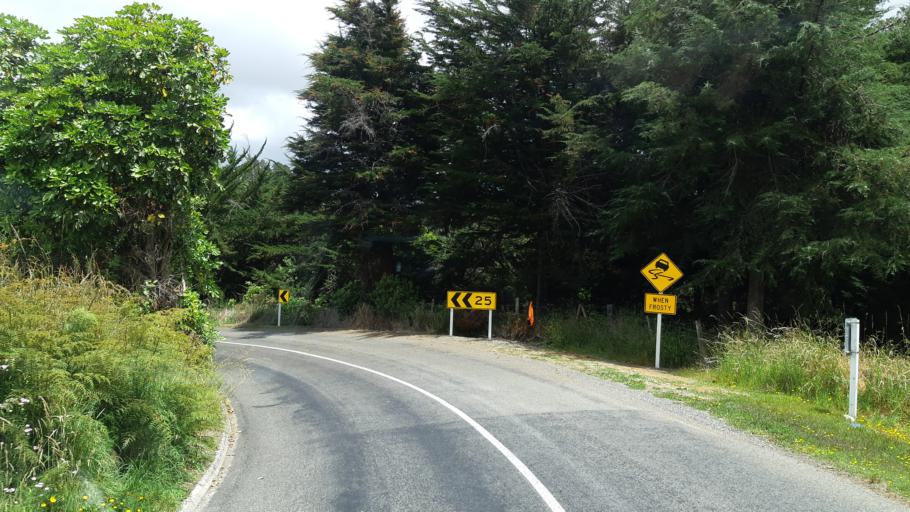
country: NZ
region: Manawatu-Wanganui
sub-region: Ruapehu District
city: Waiouru
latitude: -39.9348
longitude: 175.9214
